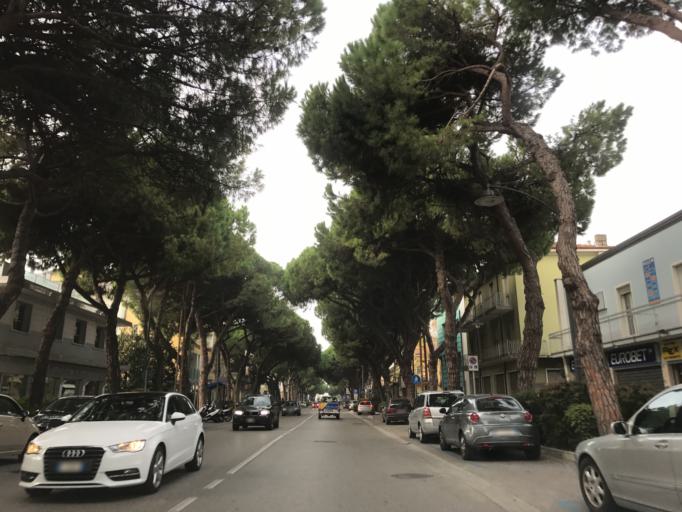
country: IT
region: Emilia-Romagna
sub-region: Forli-Cesena
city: Cesenatico
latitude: 44.1990
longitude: 12.4011
